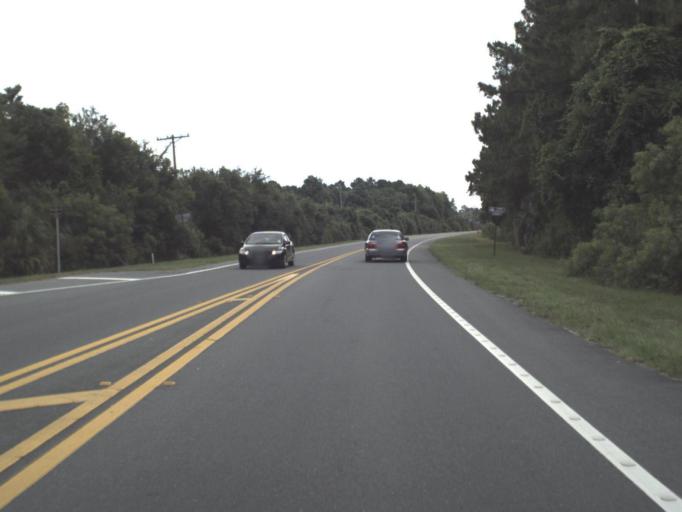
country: US
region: Florida
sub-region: Levy County
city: Chiefland
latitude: 29.1771
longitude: -83.0238
